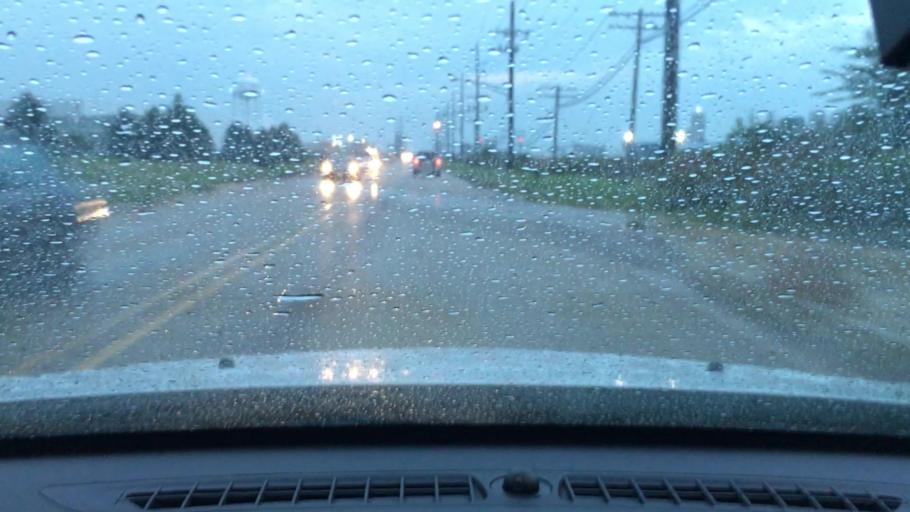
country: US
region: Illinois
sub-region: Ogle County
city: Rochelle
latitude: 41.9131
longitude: -89.0492
